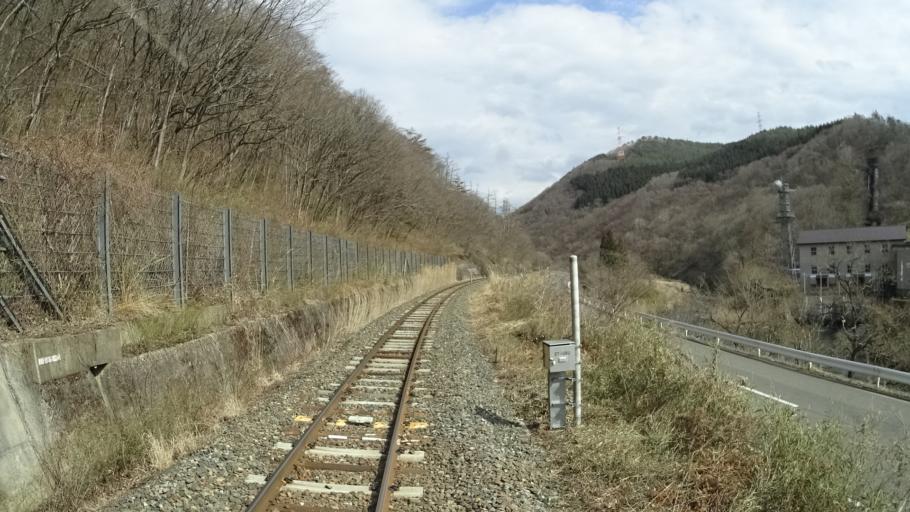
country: JP
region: Iwate
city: Hanamaki
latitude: 39.3620
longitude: 141.2861
